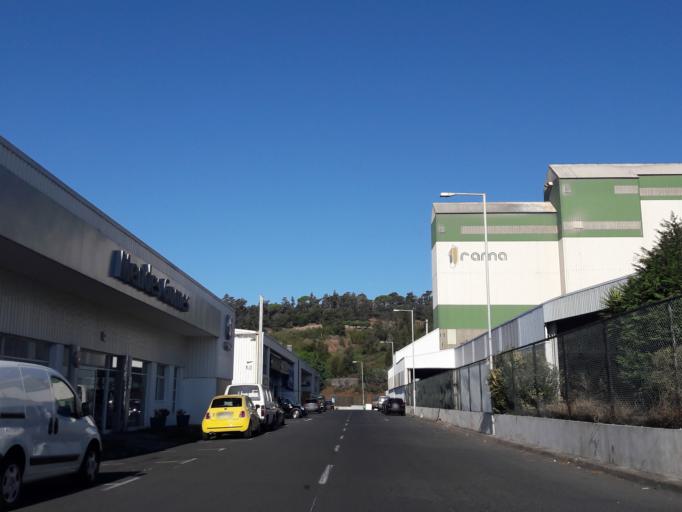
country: PT
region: Madeira
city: Canico
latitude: 32.6520
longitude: -16.8603
